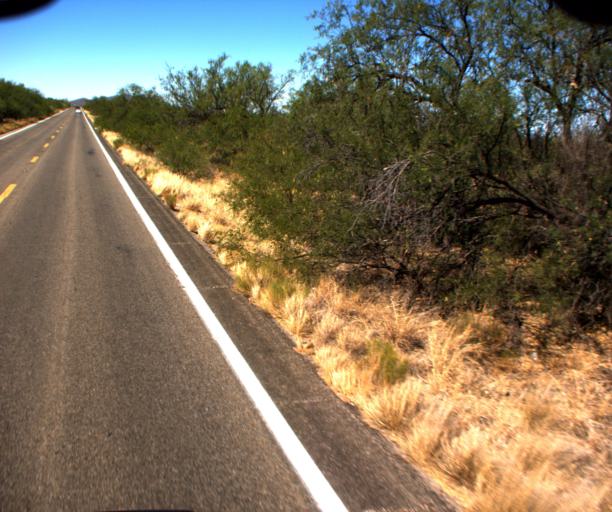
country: US
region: Arizona
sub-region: Pima County
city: Sells
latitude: 31.9584
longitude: -111.7540
